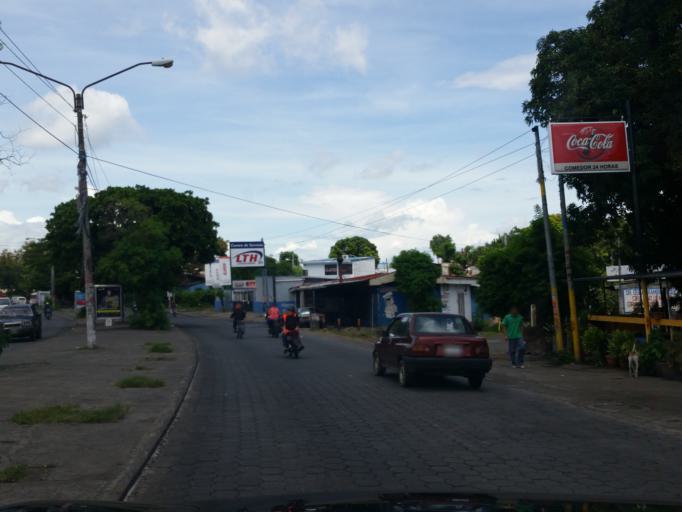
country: NI
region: Managua
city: Managua
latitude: 12.1288
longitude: -86.2327
